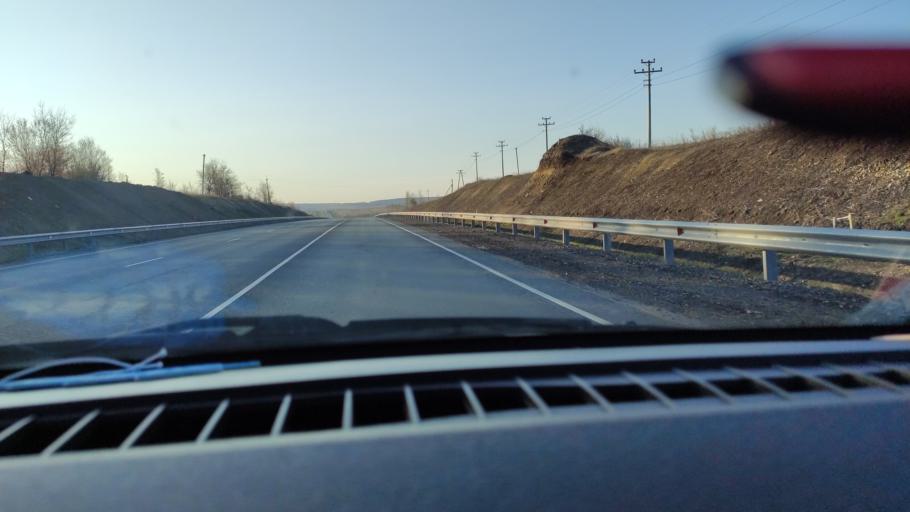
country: RU
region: Saratov
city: Shikhany
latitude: 52.1440
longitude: 47.2013
